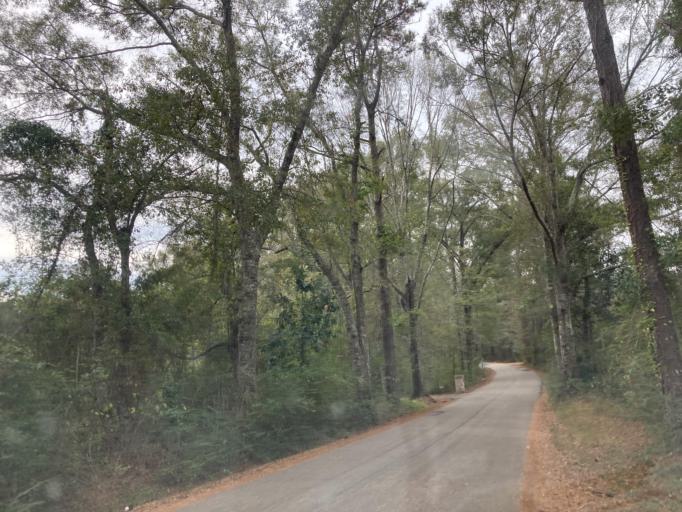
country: US
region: Mississippi
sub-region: Lamar County
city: Purvis
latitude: 31.1482
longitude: -89.4607
